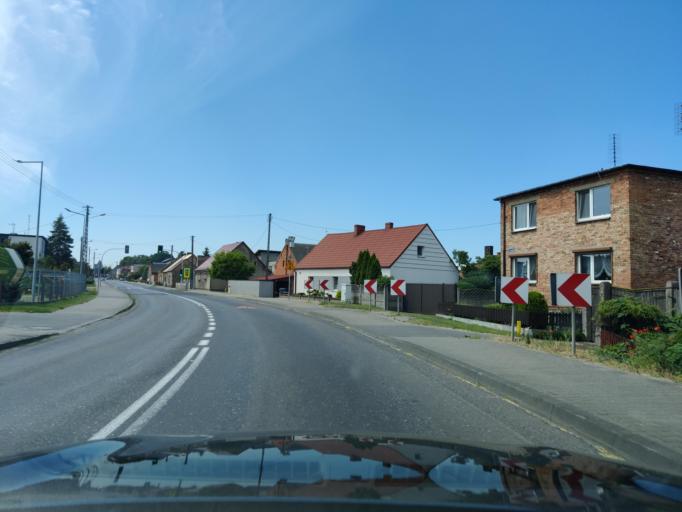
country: PL
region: Greater Poland Voivodeship
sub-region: Powiat grodziski
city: Grodzisk Wielkopolski
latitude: 52.1845
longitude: 16.3367
